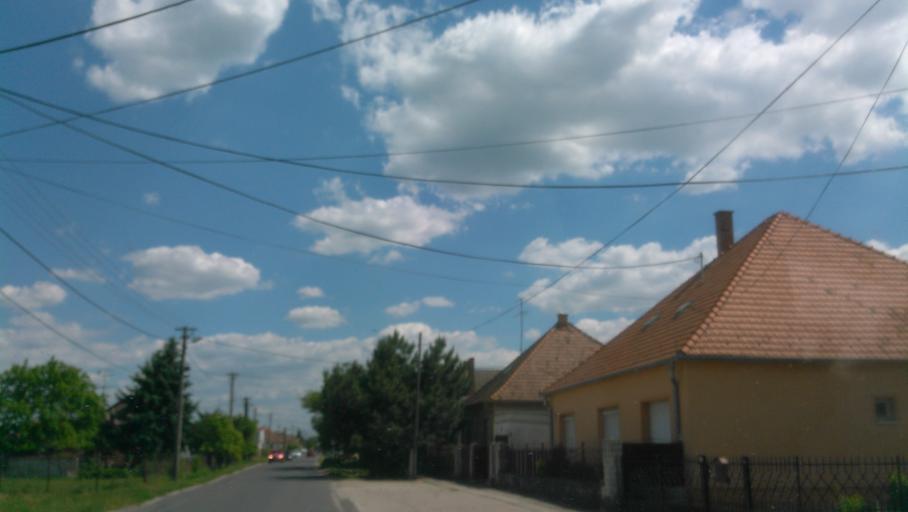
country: SK
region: Trnavsky
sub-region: Okres Dunajska Streda
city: Velky Meder
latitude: 47.8936
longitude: 17.8008
